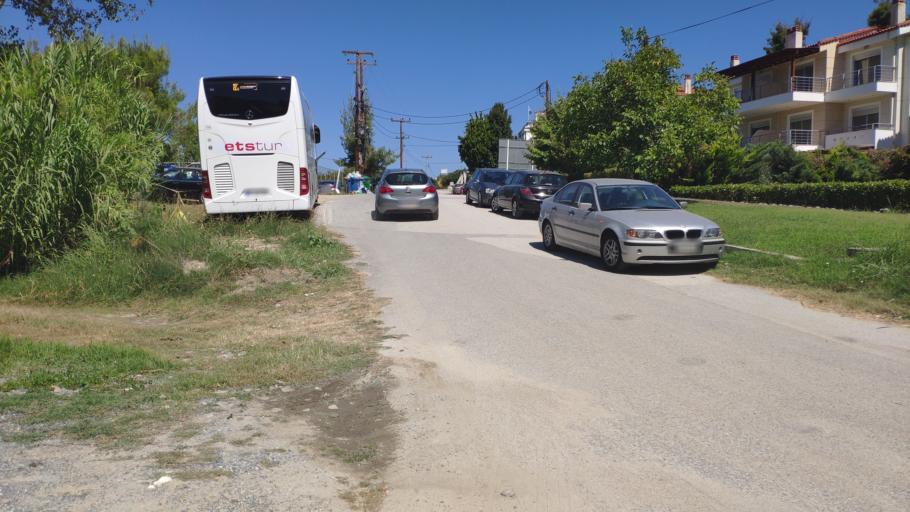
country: GR
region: Central Macedonia
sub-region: Nomos Chalkidikis
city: Kassandreia
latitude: 40.0336
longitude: 23.3620
